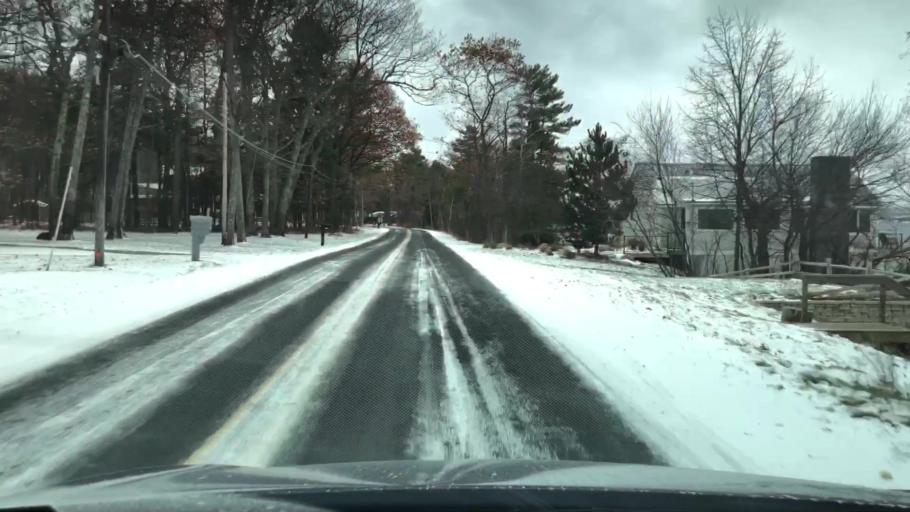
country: US
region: Michigan
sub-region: Grand Traverse County
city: Traverse City
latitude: 44.8300
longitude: -85.5647
